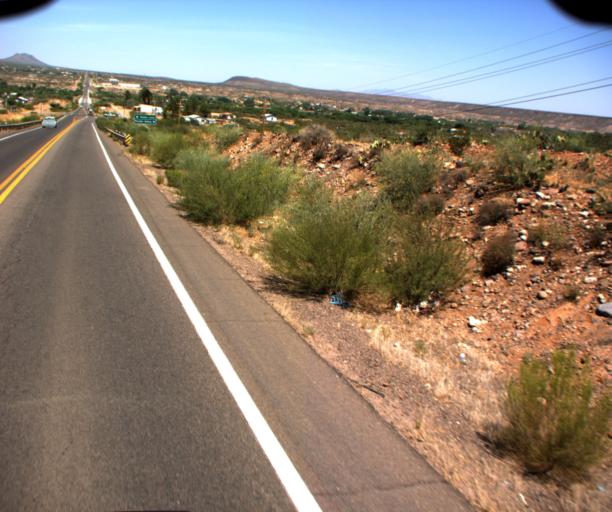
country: US
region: Arizona
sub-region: Gila County
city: Peridot
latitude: 33.2940
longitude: -110.4420
